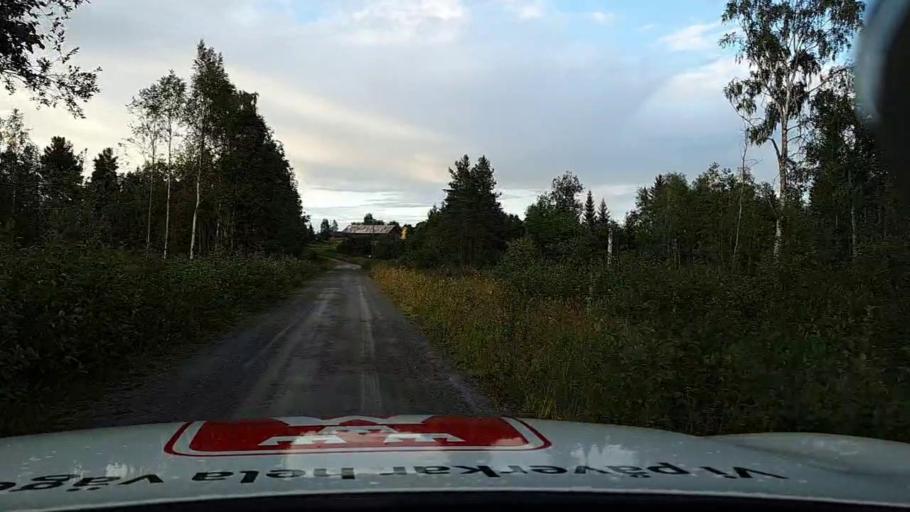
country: SE
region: Jaemtland
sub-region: Bergs Kommun
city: Hoverberg
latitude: 62.8694
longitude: 14.6204
